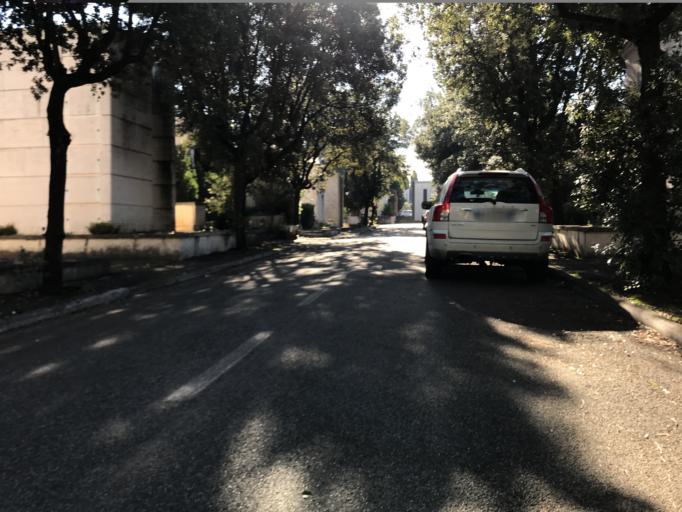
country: IT
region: Latium
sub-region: Citta metropolitana di Roma Capitale
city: Rome
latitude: 41.9002
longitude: 12.5213
